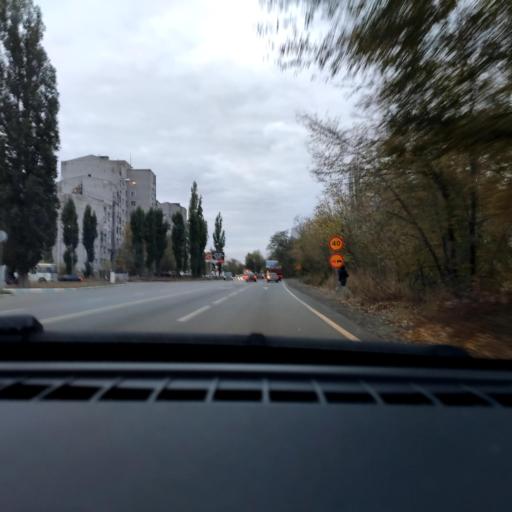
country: RU
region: Voronezj
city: Maslovka
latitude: 51.6016
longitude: 39.2533
